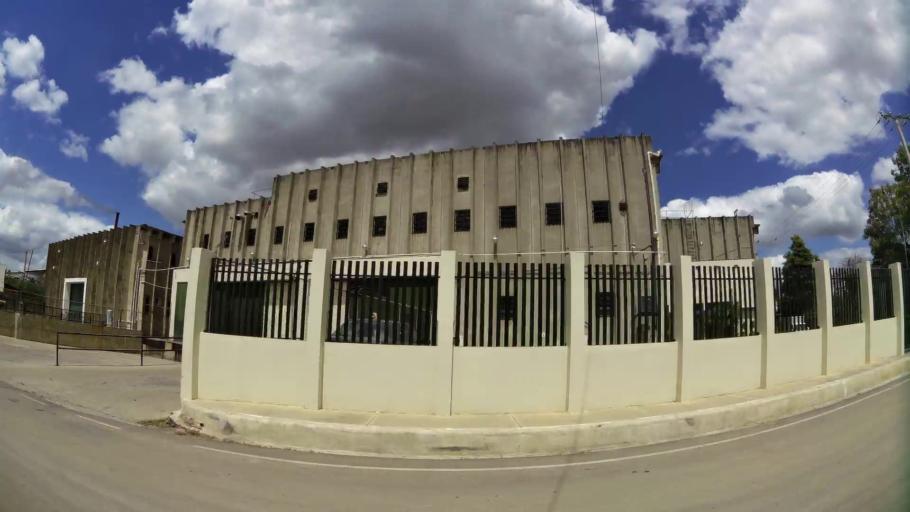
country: DO
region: Nacional
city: Ensanche Luperon
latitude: 18.5128
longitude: -69.9041
